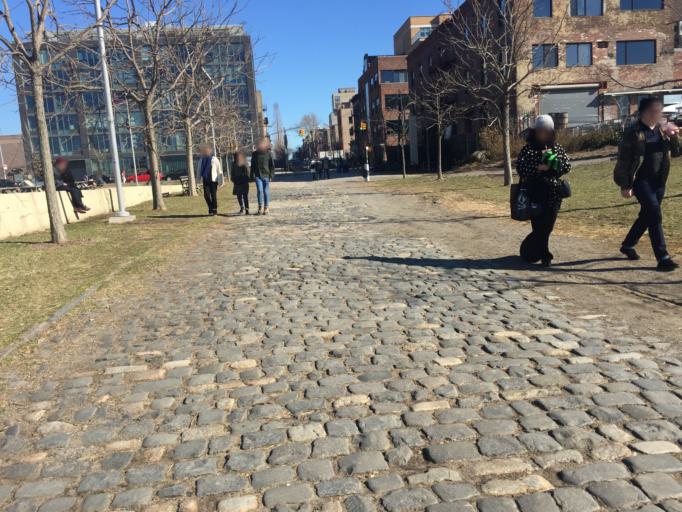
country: US
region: New York
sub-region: Queens County
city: Long Island City
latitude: 40.7214
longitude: -73.9618
